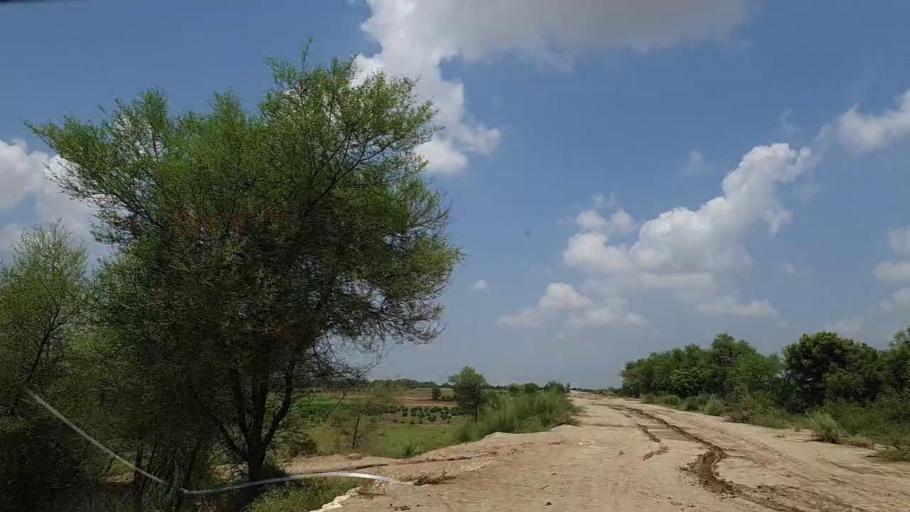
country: PK
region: Sindh
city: Tharu Shah
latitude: 26.9404
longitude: 68.0123
